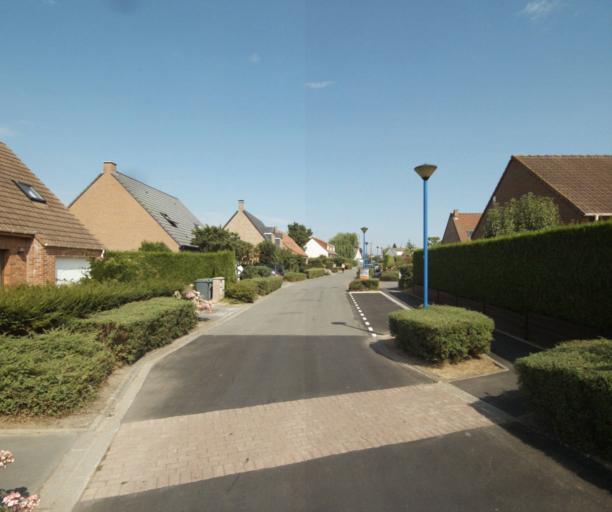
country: FR
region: Nord-Pas-de-Calais
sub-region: Departement du Nord
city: Sainghin-en-Weppes
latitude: 50.5666
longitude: 2.8984
